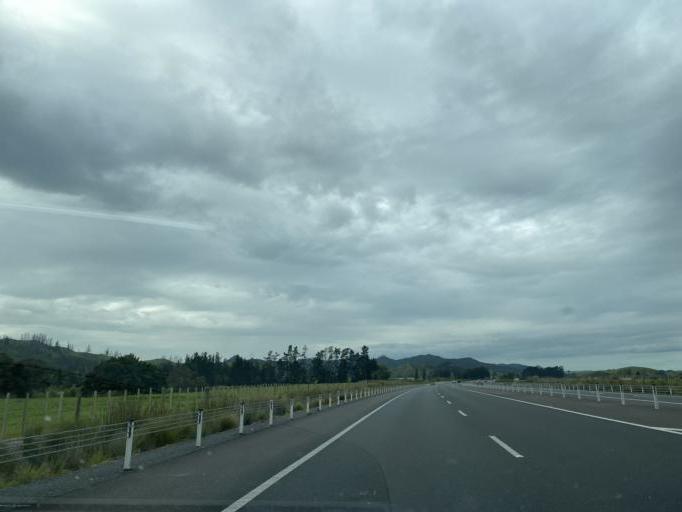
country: NZ
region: Waikato
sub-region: Waikato District
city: Ngaruawahia
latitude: -37.6094
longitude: 175.2046
